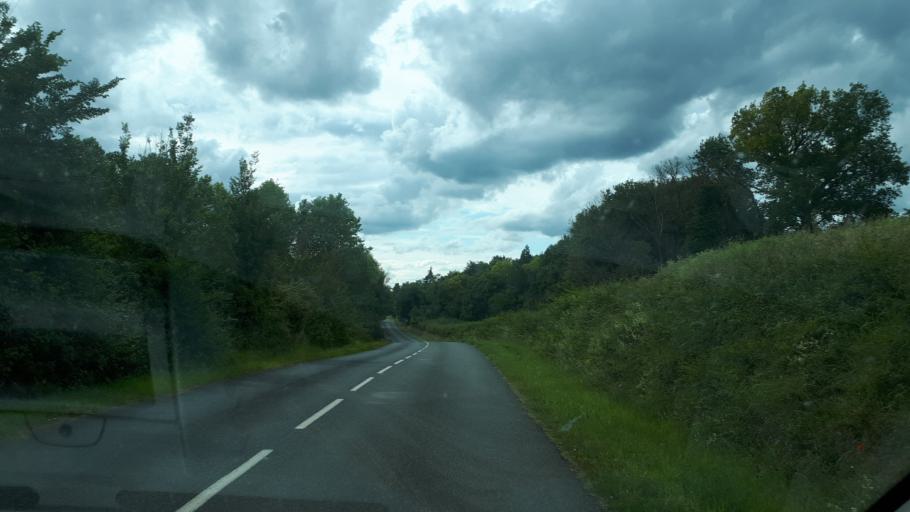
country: FR
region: Centre
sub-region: Departement du Cher
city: Gracay
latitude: 47.1385
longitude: 1.8639
